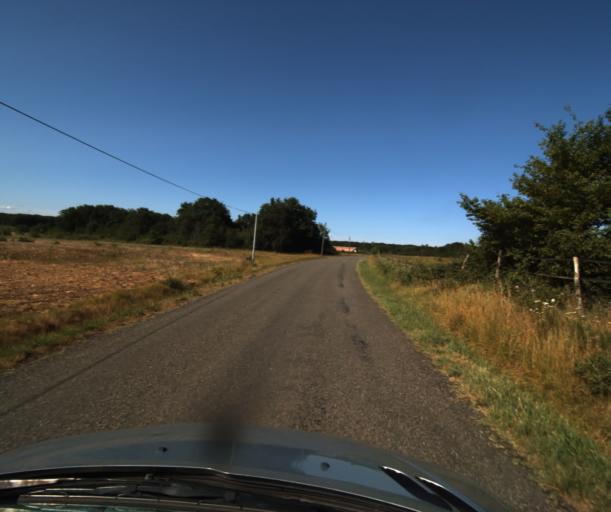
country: FR
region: Midi-Pyrenees
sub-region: Departement du Tarn-et-Garonne
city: Campsas
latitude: 43.9251
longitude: 1.2940
